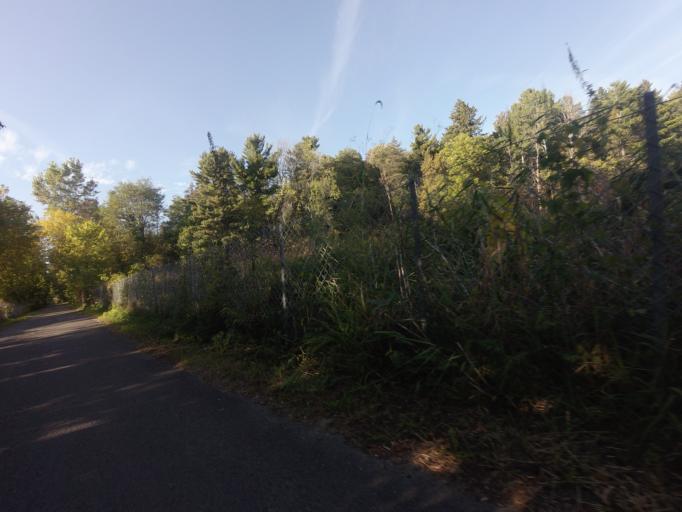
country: CA
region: Quebec
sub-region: Laurentides
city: Saint-Jerome
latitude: 45.7357
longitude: -73.9502
